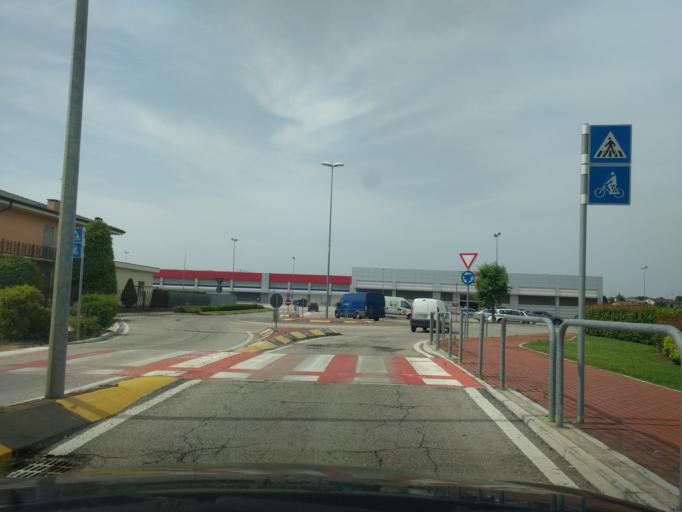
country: IT
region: Veneto
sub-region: Provincia di Verona
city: Legnago
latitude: 45.1854
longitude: 11.2725
